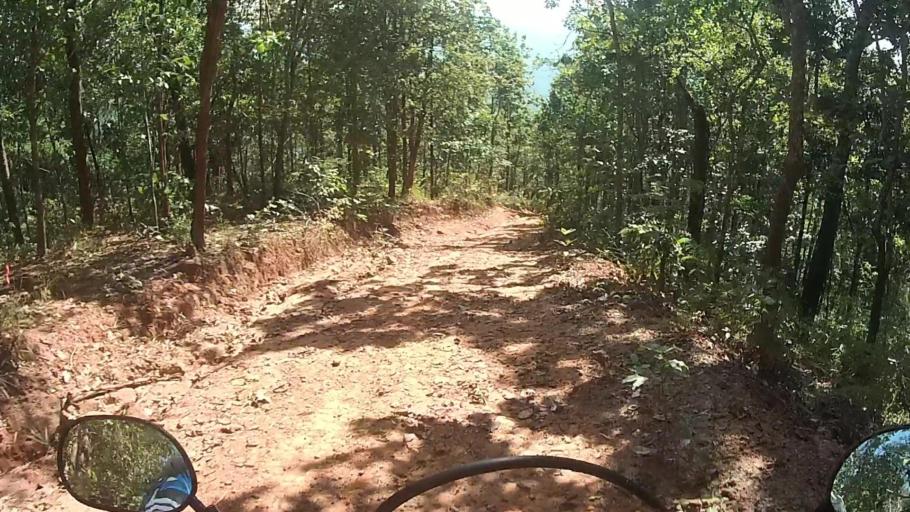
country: TH
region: Chiang Mai
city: Mae On
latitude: 19.0287
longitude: 99.2959
